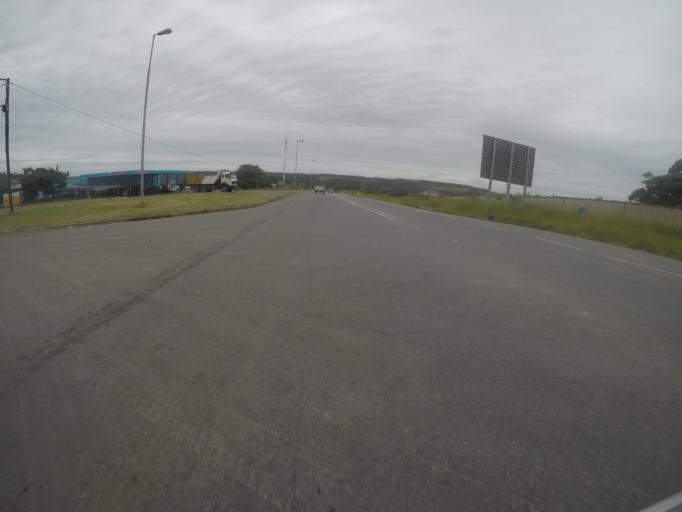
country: ZA
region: Eastern Cape
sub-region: Buffalo City Metropolitan Municipality
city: East London
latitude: -32.9509
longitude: 27.9187
